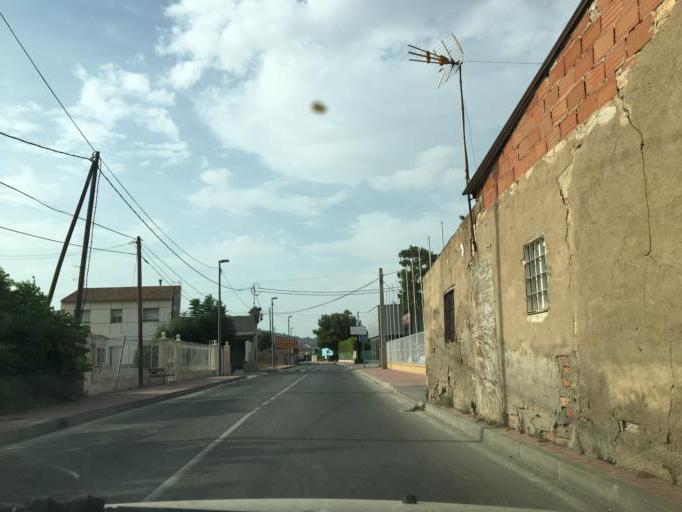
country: ES
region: Murcia
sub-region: Murcia
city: Murcia
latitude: 38.0101
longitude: -1.0808
